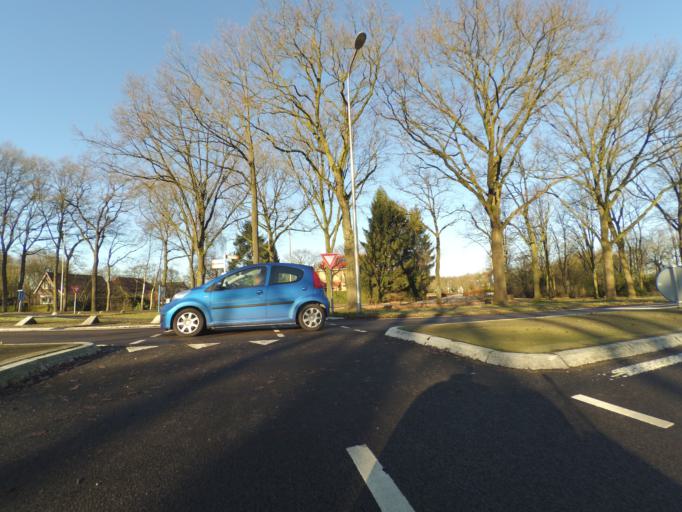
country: NL
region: Gelderland
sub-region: Gemeente Putten
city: Putten
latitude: 52.2638
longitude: 5.6032
